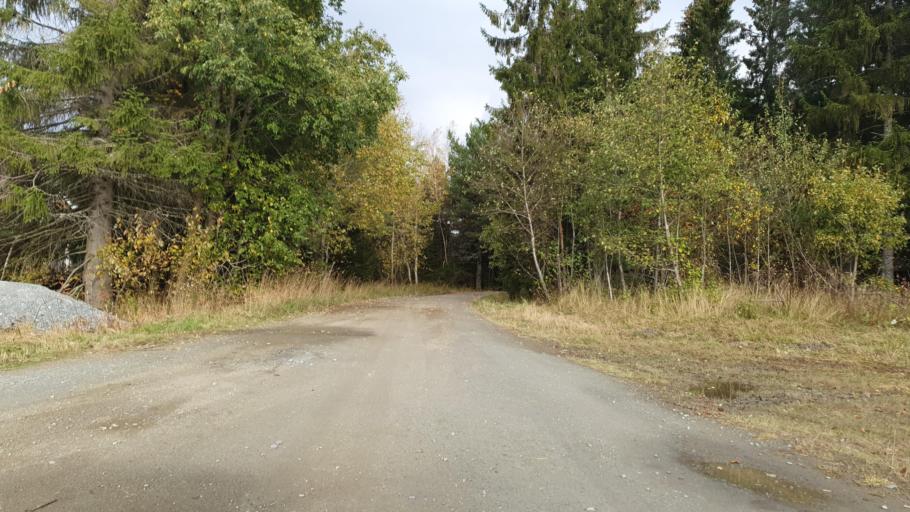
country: NO
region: Sor-Trondelag
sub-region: Klaebu
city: Klaebu
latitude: 63.2957
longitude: 10.4630
